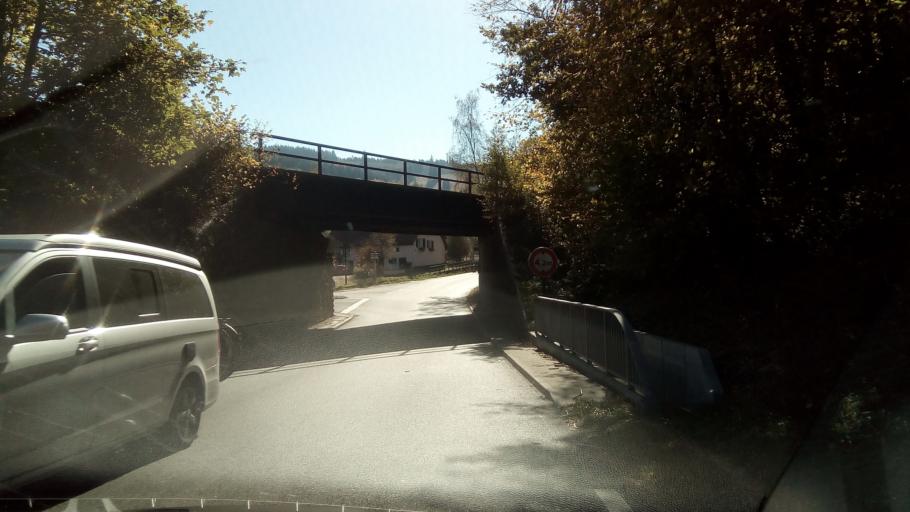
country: FR
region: Alsace
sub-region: Departement du Bas-Rhin
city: Rothau
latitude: 48.4260
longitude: 7.1843
